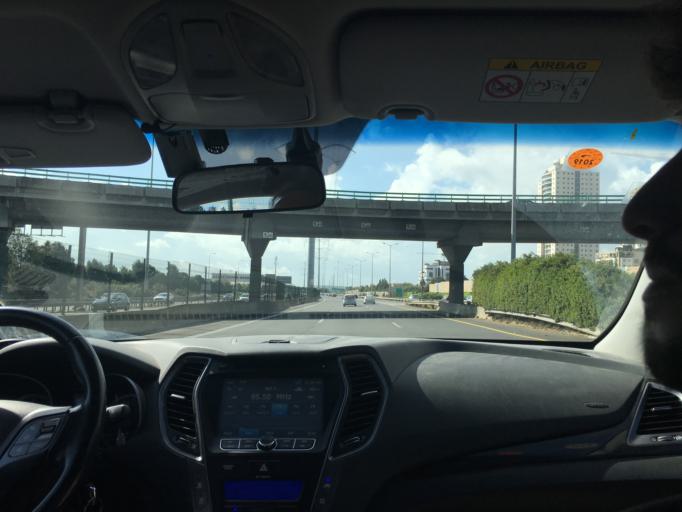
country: IL
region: Tel Aviv
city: Bene Beraq
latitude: 32.0645
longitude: 34.8378
